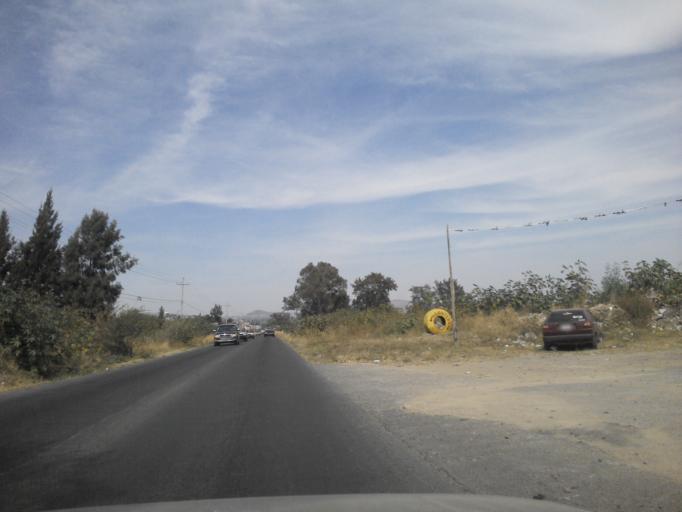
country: MX
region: Jalisco
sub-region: Tlajomulco de Zuniga
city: Lomas del Sur
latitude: 20.5037
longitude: -103.4146
